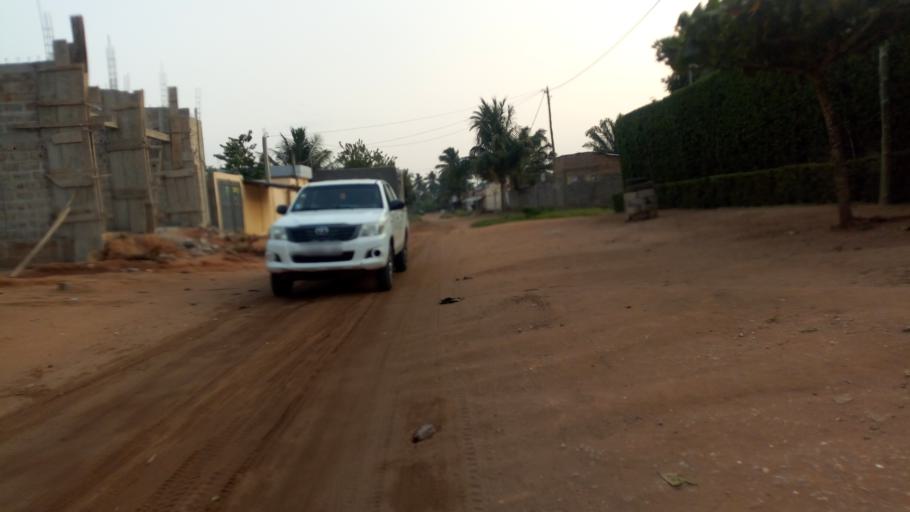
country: TG
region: Maritime
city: Lome
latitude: 6.1921
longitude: 1.1404
